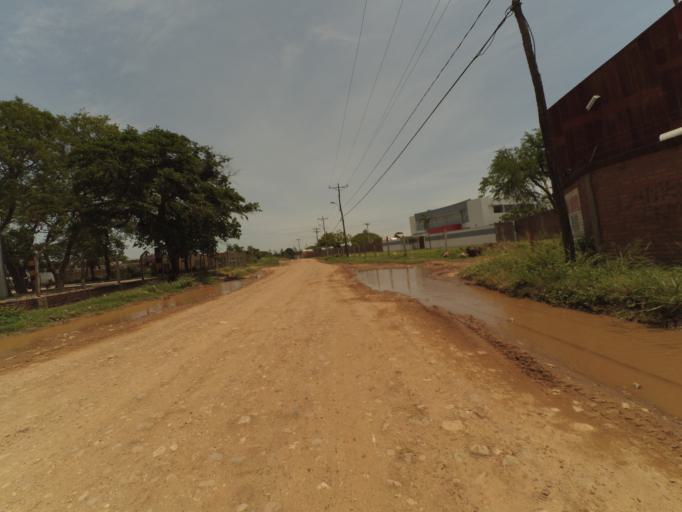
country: BO
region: Santa Cruz
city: Santa Cruz de la Sierra
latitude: -17.8409
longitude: -63.2442
